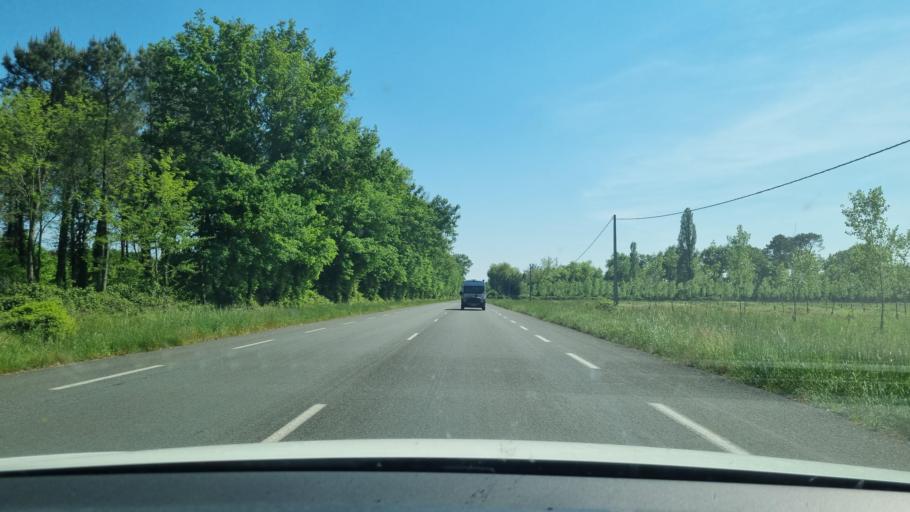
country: FR
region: Aquitaine
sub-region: Departement de la Gironde
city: Prechac
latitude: 44.2453
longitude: -0.2610
